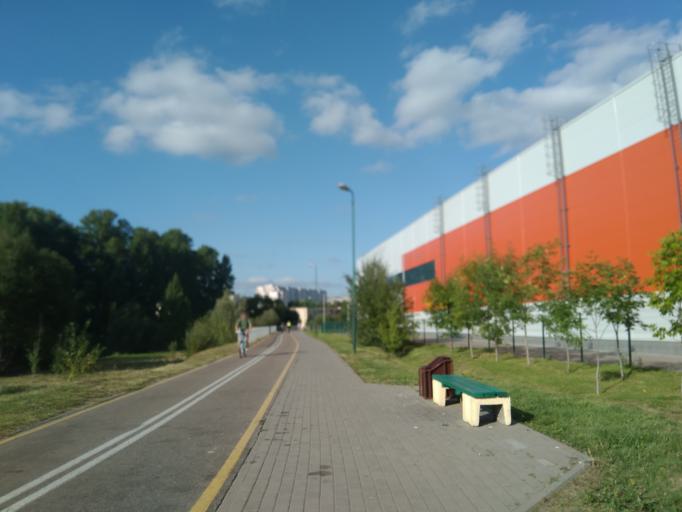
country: BY
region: Minsk
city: Minsk
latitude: 53.8669
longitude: 27.5890
